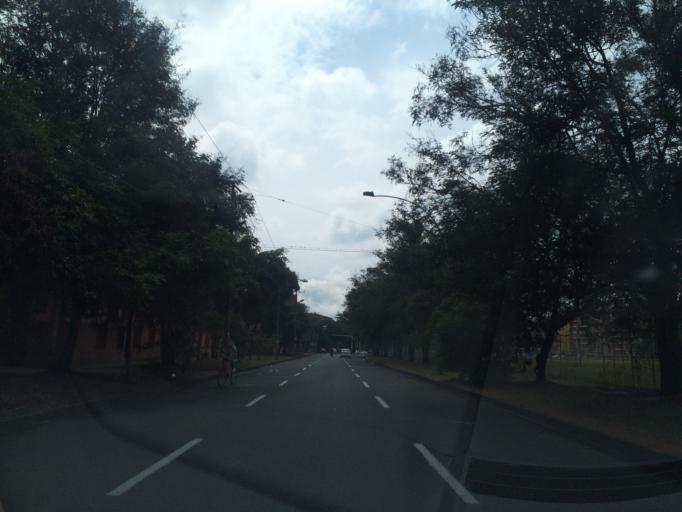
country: CO
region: Valle del Cauca
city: Cali
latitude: 3.3797
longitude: -76.5308
